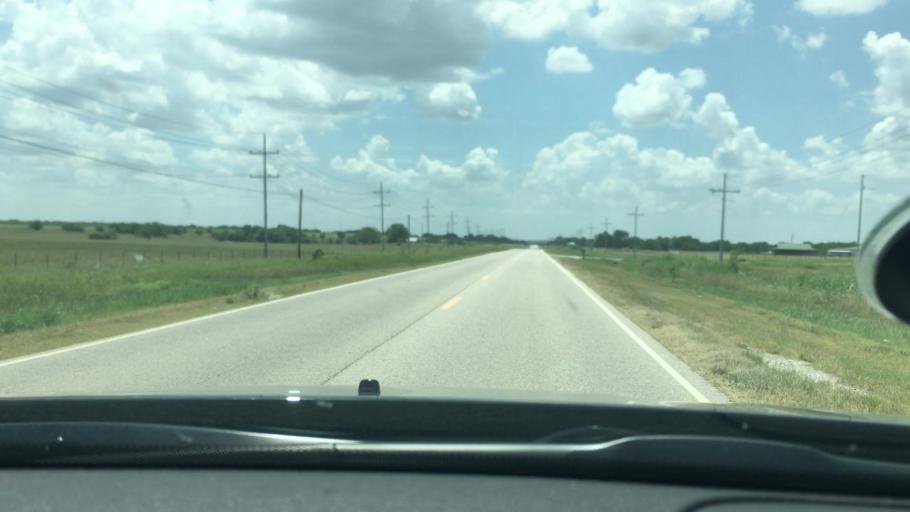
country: US
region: Oklahoma
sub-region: Pontotoc County
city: Ada
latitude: 34.6437
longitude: -96.6349
